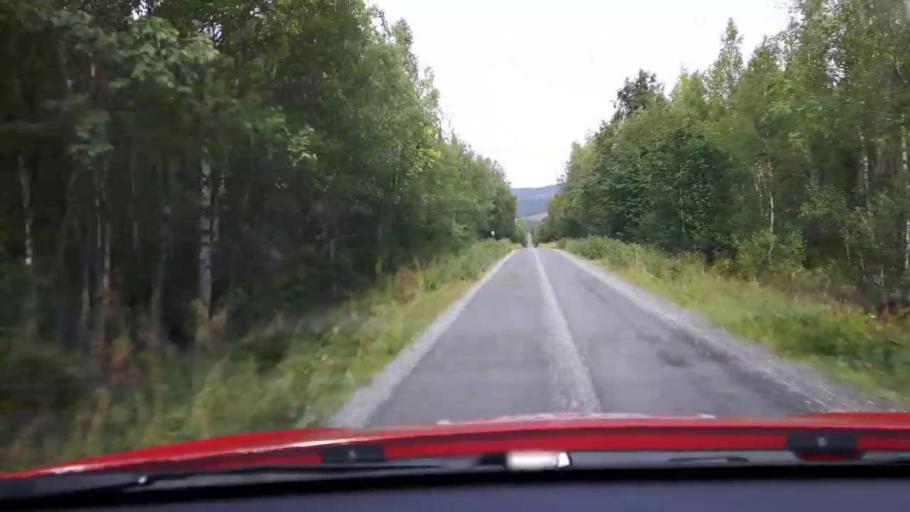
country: SE
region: Jaemtland
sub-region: Are Kommun
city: Are
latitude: 63.7890
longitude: 13.1059
